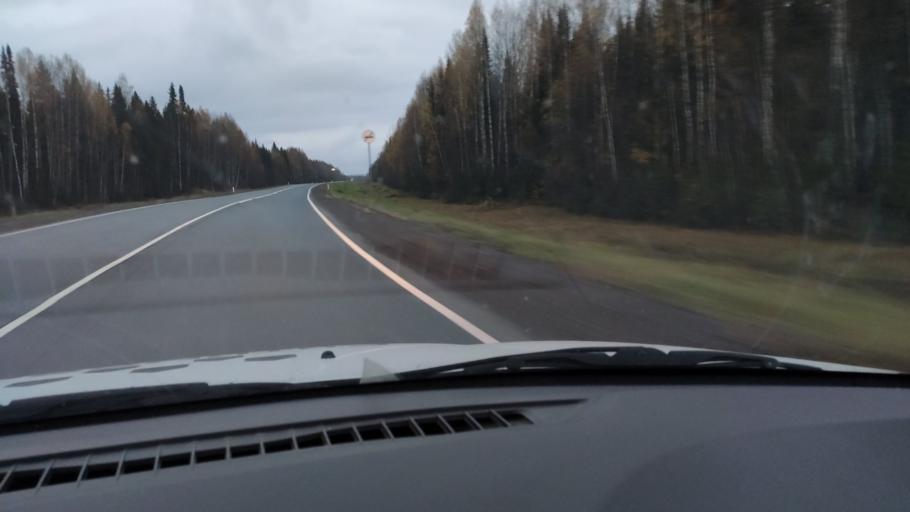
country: RU
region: Kirov
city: Kostino
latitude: 58.8583
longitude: 53.1046
